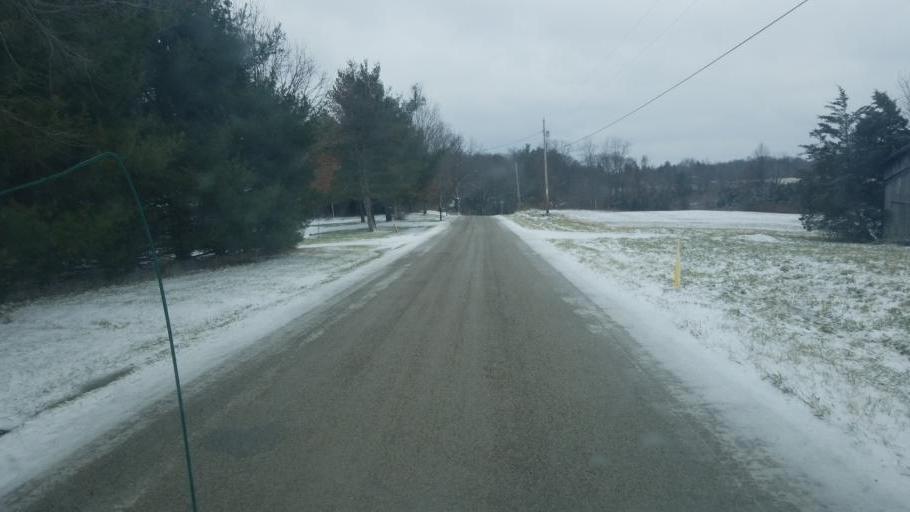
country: US
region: Ohio
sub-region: Delaware County
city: Sunbury
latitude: 40.3542
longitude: -82.8186
